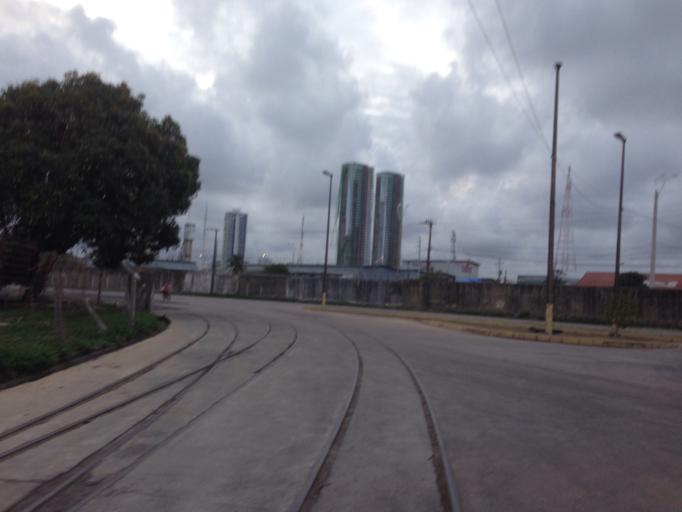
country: BR
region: Pernambuco
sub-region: Recife
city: Recife
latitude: -8.0500
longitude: -34.8691
